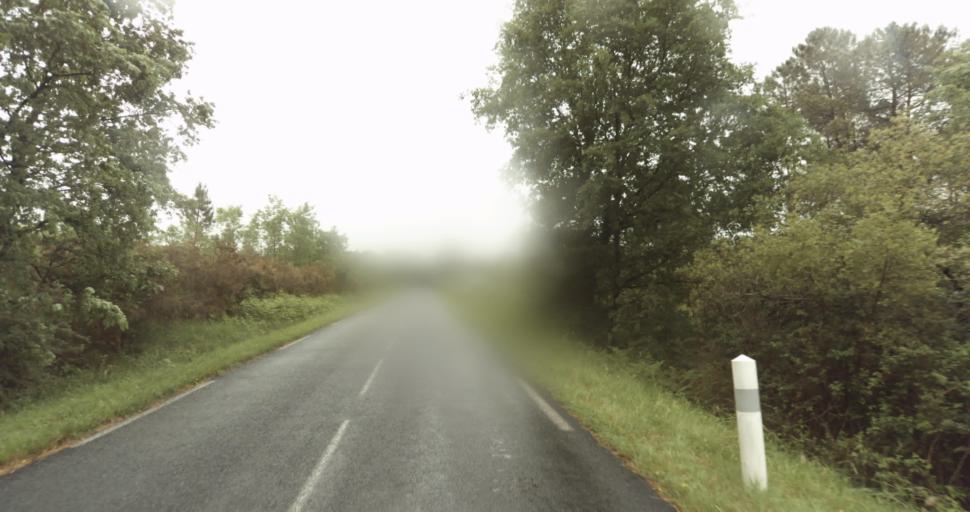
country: FR
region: Aquitaine
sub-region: Departement de la Dordogne
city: Beaumont-du-Perigord
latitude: 44.7940
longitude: 0.8500
